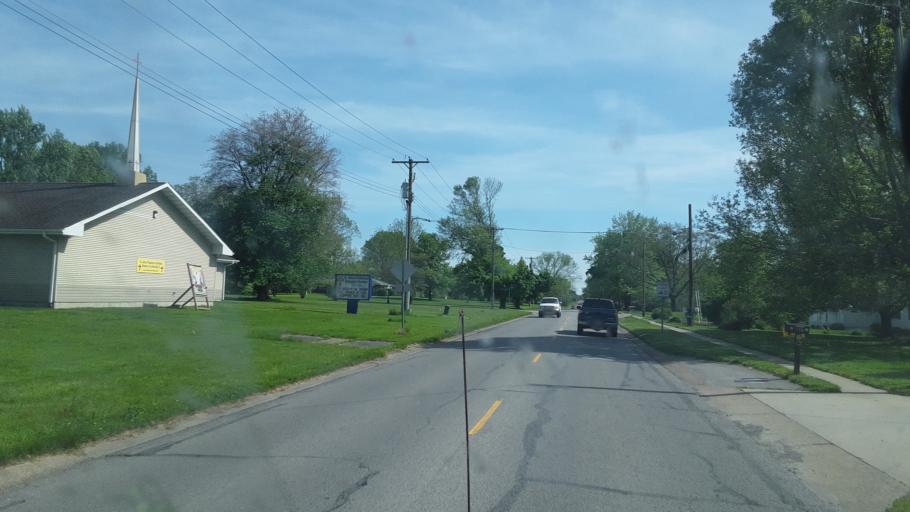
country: US
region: Illinois
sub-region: Jackson County
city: Carbondale
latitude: 37.7233
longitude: -89.1851
